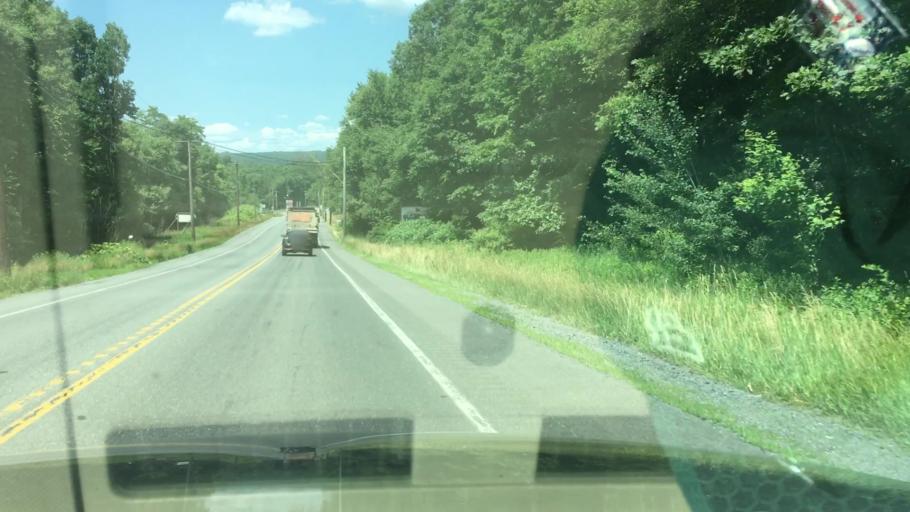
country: US
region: Pennsylvania
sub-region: Northumberland County
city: Kulpmont
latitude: 40.7766
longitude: -76.4455
